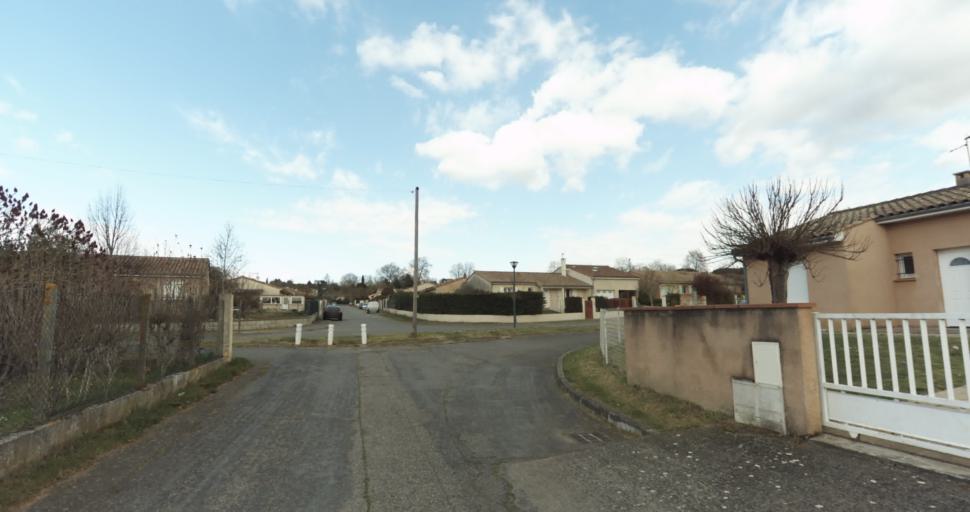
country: FR
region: Midi-Pyrenees
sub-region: Departement de la Haute-Garonne
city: Auterive
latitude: 43.3545
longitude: 1.4823
